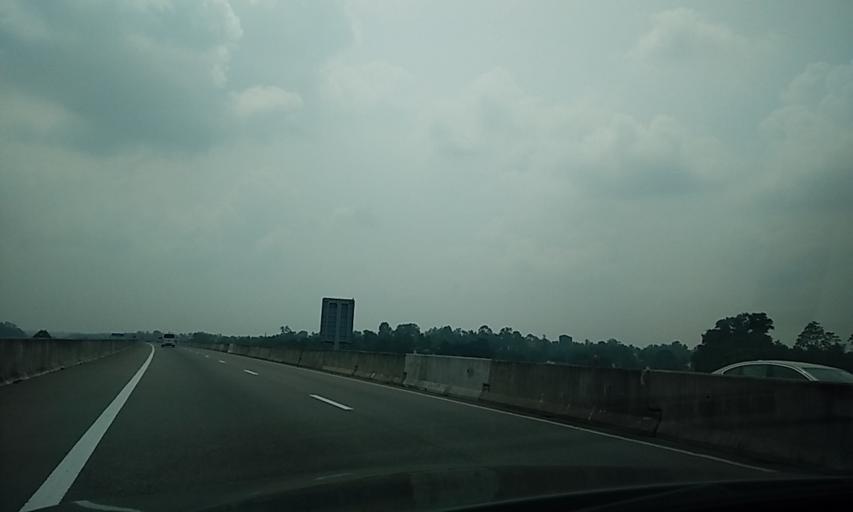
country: LK
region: Western
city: Mulleriyawa
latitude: 6.9109
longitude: 79.9817
